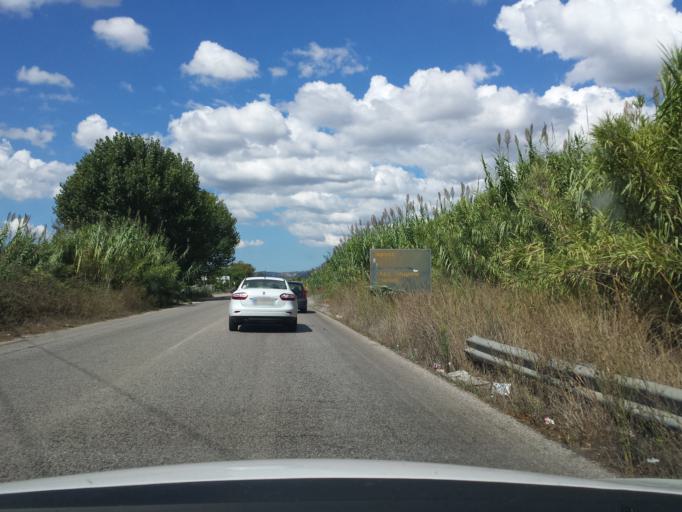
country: GR
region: West Greece
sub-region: Nomos Ileias
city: Epitalion
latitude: 37.6502
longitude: 21.4711
